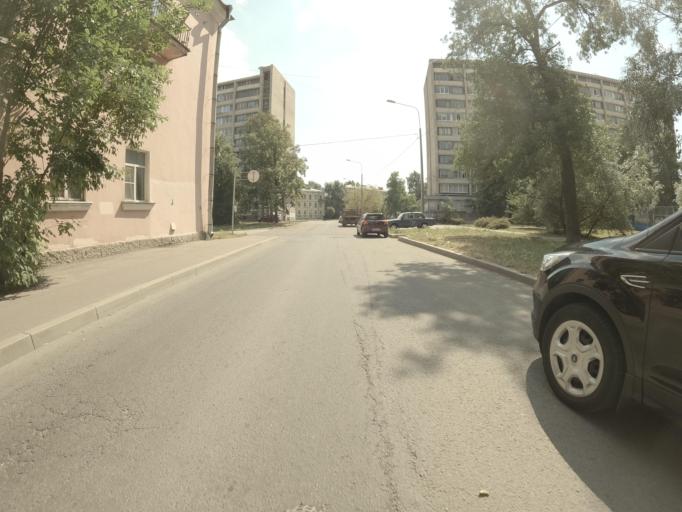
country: RU
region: St.-Petersburg
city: Avtovo
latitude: 59.8927
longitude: 30.2615
